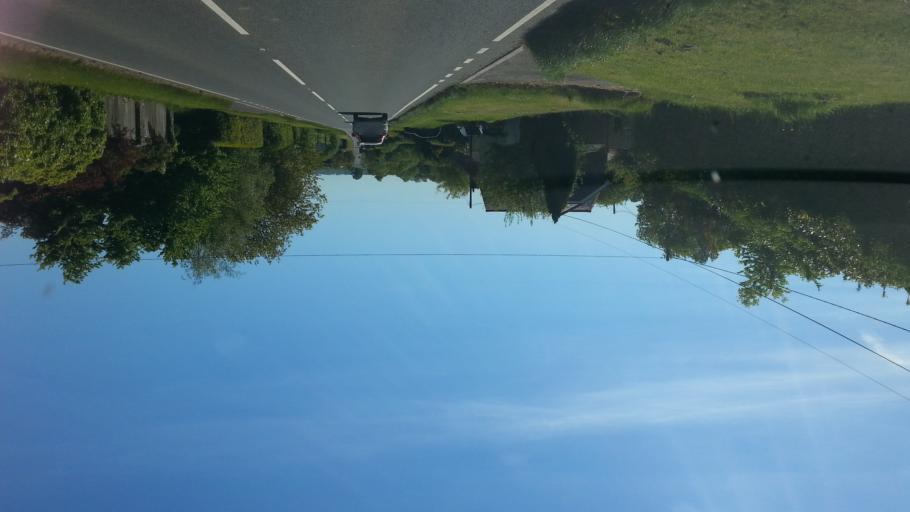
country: GB
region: England
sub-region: Dorset
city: Shaftesbury
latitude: 51.0075
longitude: -2.2318
